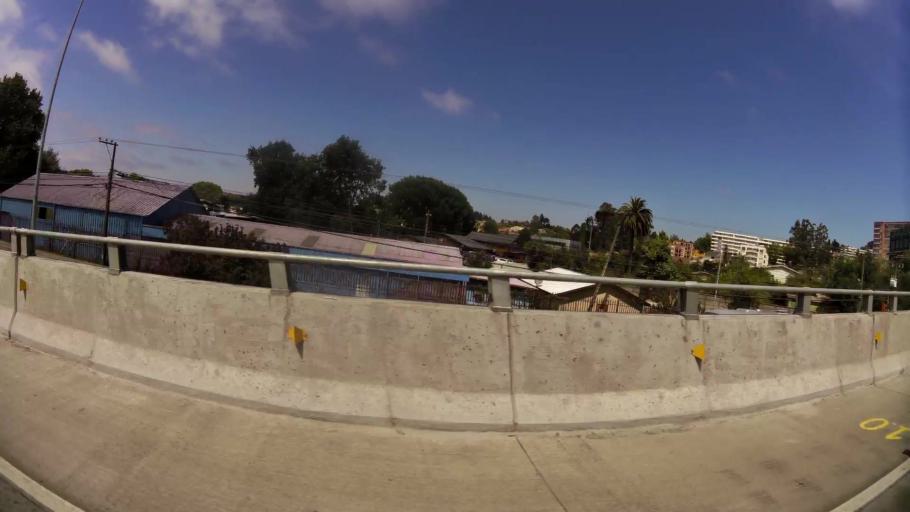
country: CL
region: Biobio
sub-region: Provincia de Concepcion
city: Concepcion
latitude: -36.7888
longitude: -73.0610
